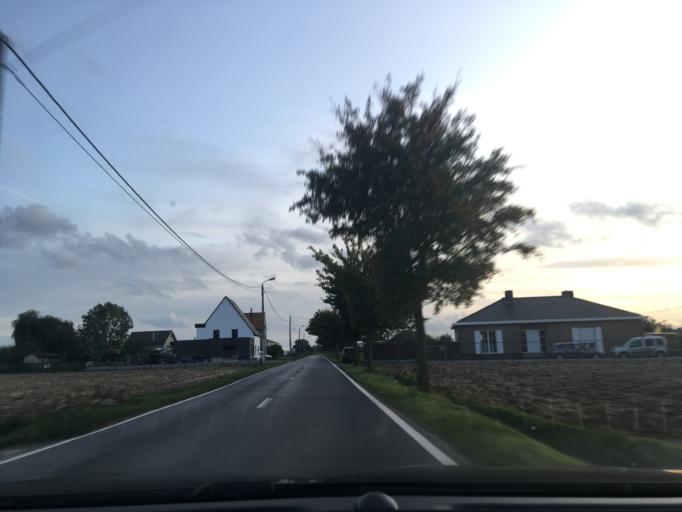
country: BE
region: Flanders
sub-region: Provincie West-Vlaanderen
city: Moorslede
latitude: 50.9316
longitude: 3.0531
